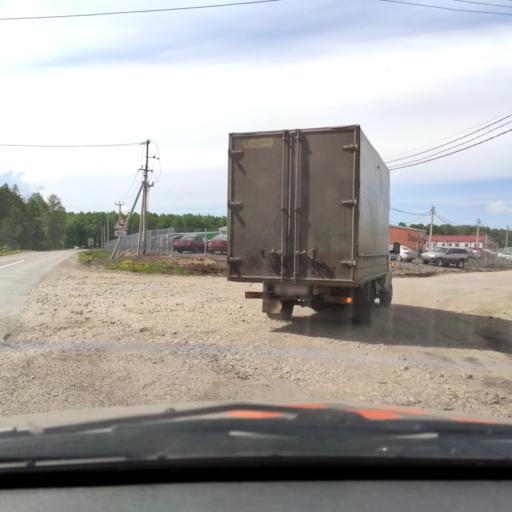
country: RU
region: Bashkortostan
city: Avdon
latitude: 54.6569
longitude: 55.7012
